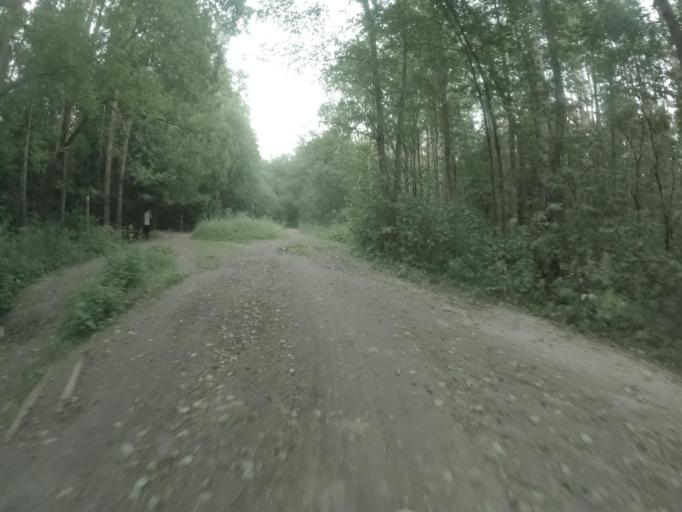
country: RU
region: St.-Petersburg
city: Krasnogvargeisky
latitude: 59.9589
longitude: 30.5320
